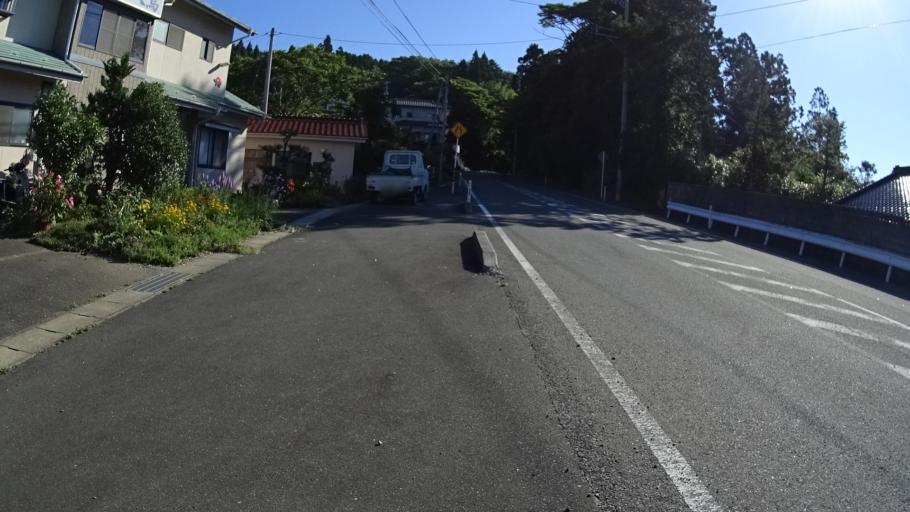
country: JP
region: Iwate
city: Ofunato
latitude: 38.8647
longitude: 141.6192
